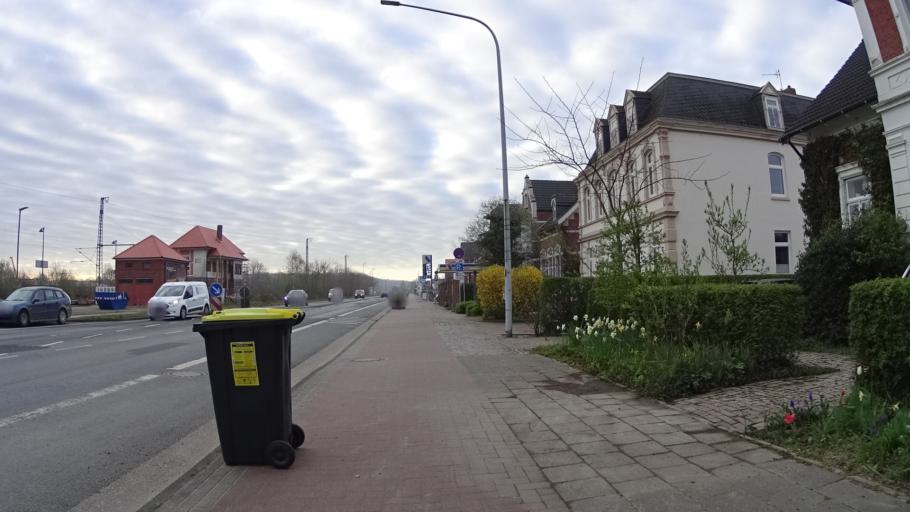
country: DE
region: Lower Saxony
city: Norden
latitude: 53.5863
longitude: 7.2210
